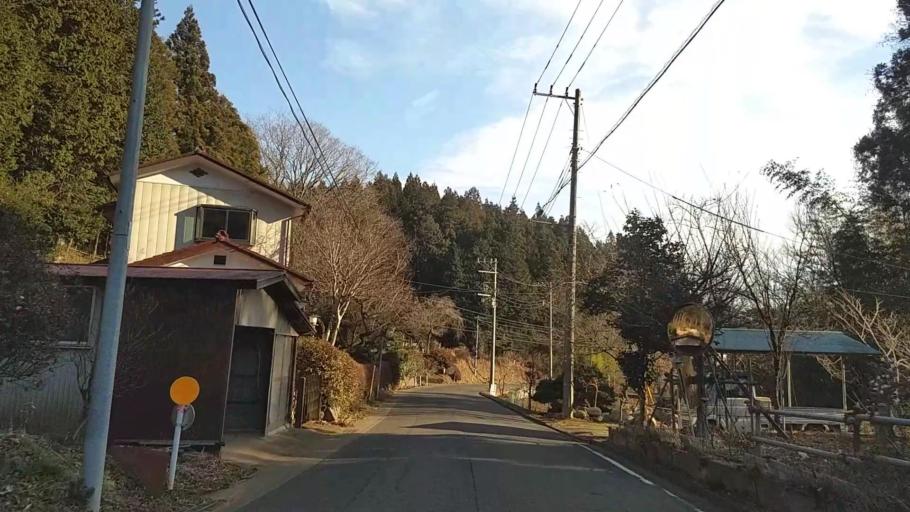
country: JP
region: Yamanashi
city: Uenohara
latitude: 35.5517
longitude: 139.2140
